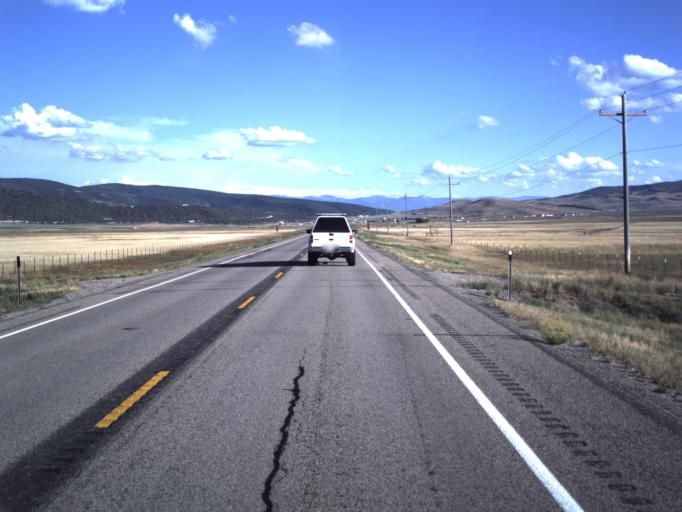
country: US
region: Utah
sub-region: Sanpete County
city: Fairview
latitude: 39.7999
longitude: -111.5010
